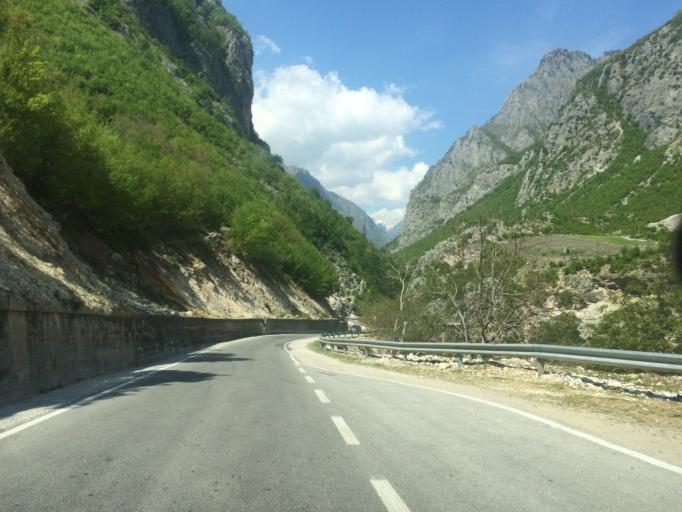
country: AL
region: Kukes
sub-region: Rrethi i Tropojes
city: Bajram Curri
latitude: 42.3874
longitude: 20.0751
